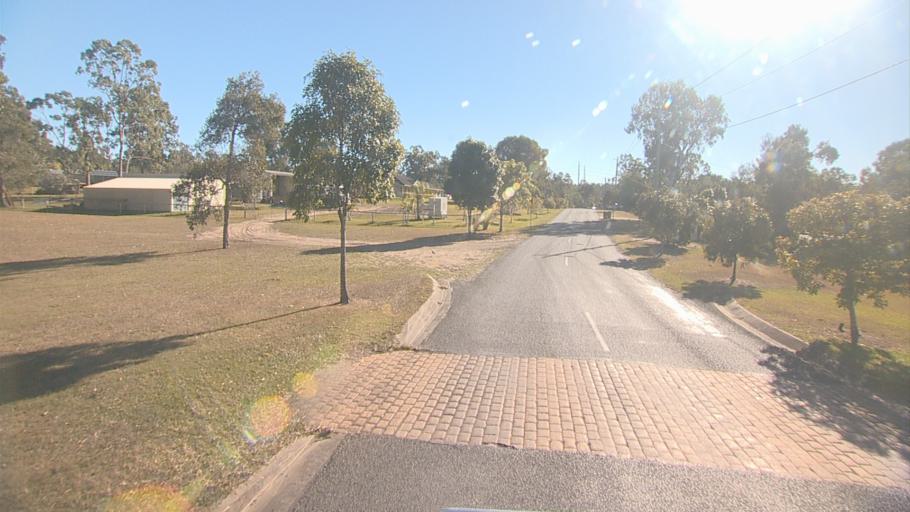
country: AU
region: Queensland
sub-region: Logan
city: North Maclean
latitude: -27.7434
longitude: 152.9677
